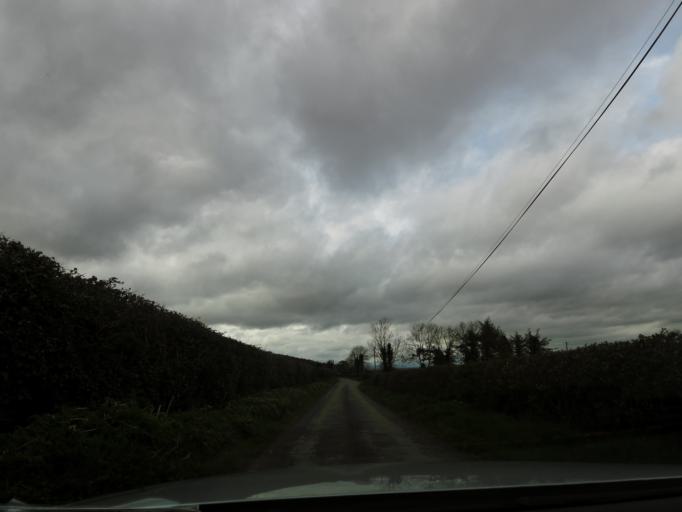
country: IE
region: Leinster
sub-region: Kilkenny
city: Kilkenny
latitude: 52.6908
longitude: -7.2923
